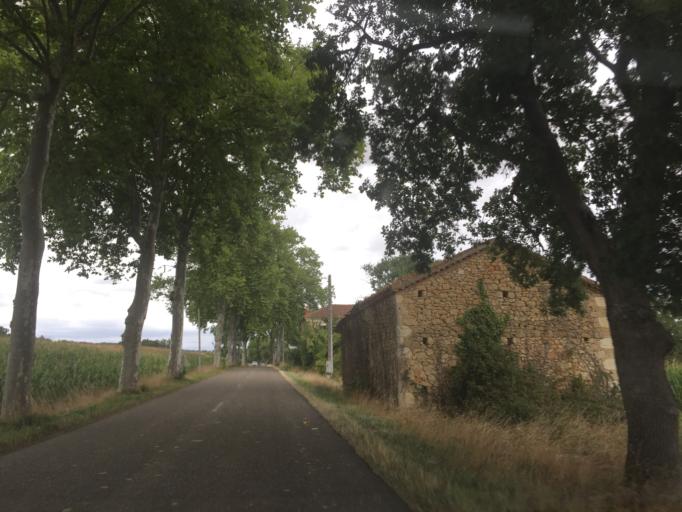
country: FR
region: Midi-Pyrenees
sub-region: Departement du Gers
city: Vic-Fezensac
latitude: 43.7421
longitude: 0.3780
